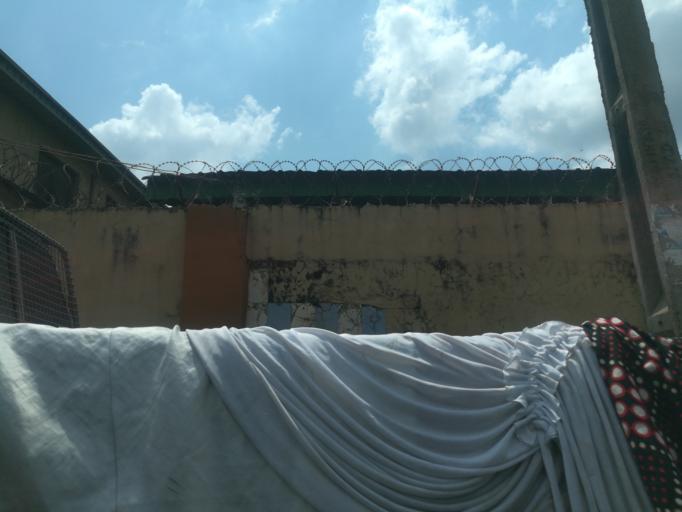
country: NG
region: Oyo
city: Ibadan
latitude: 7.4025
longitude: 3.9414
